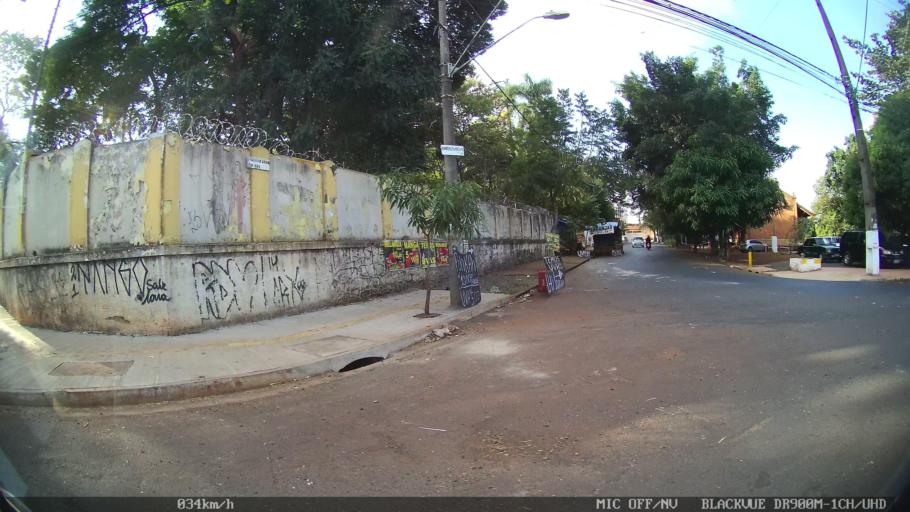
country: BR
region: Sao Paulo
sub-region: Ribeirao Preto
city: Ribeirao Preto
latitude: -21.1596
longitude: -47.8145
